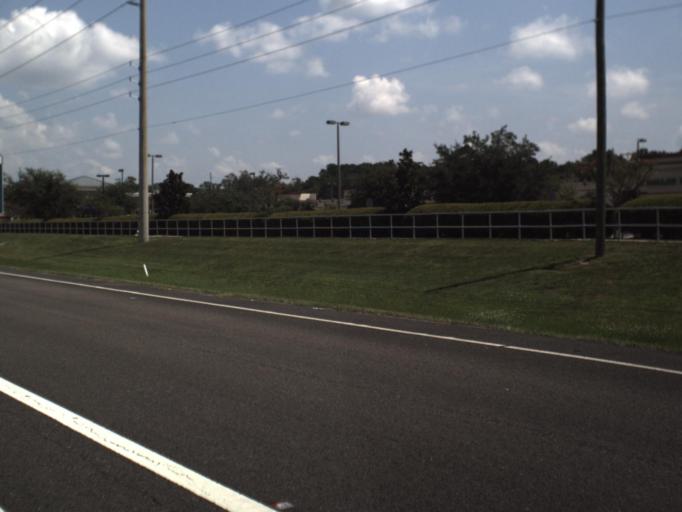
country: US
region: Florida
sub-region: Hillsborough County
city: Cheval
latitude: 28.1249
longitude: -82.5023
